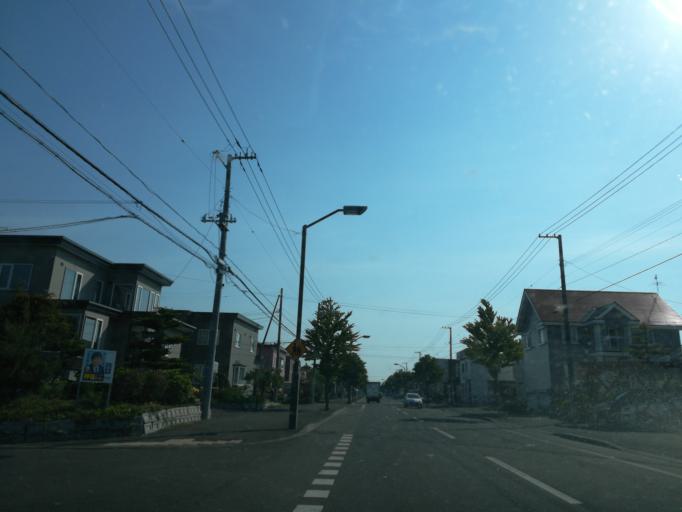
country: JP
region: Hokkaido
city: Iwamizawa
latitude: 43.1476
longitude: 141.6605
